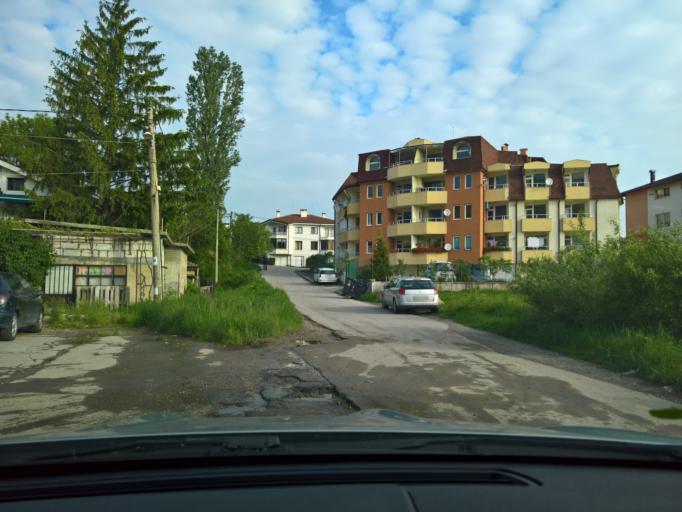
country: BG
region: Sofia-Capital
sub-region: Stolichna Obshtina
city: Sofia
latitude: 42.6672
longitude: 23.2481
